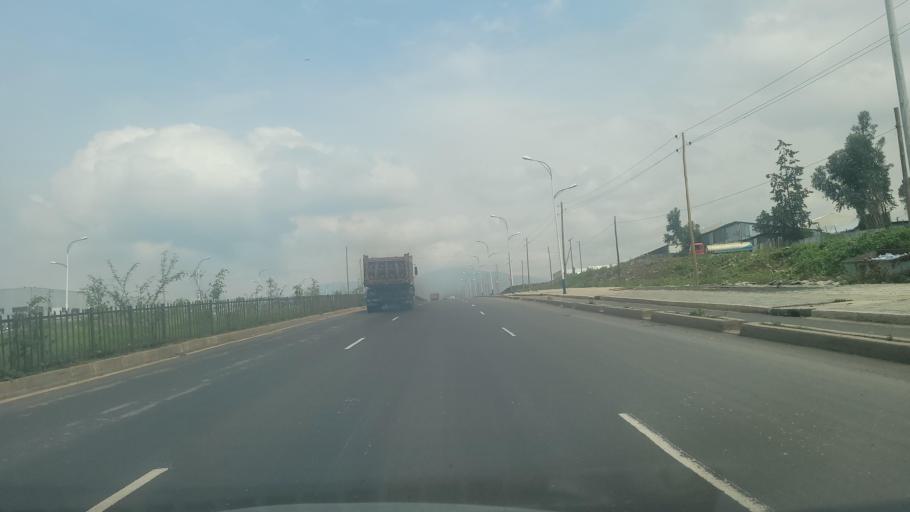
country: ET
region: Adis Abeba
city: Addis Ababa
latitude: 8.9497
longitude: 38.7072
